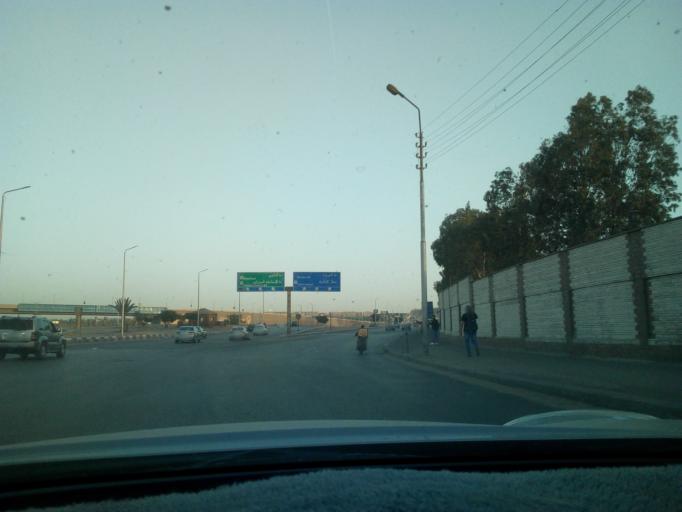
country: EG
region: Muhafazat al Qalyubiyah
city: Al Khankah
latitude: 30.1168
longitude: 31.3638
